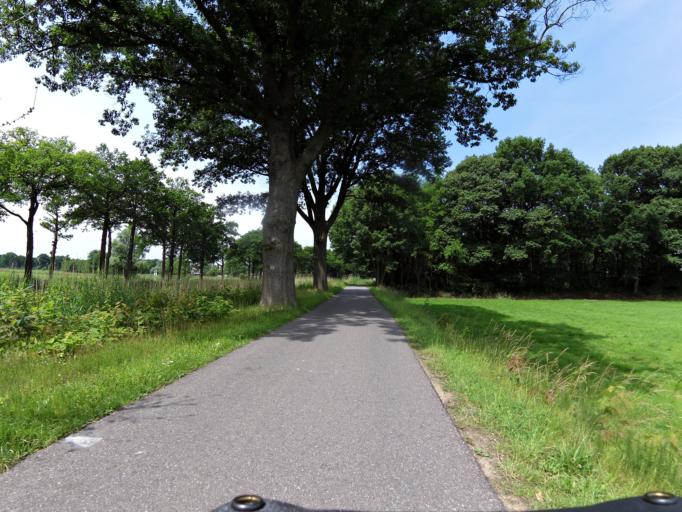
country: NL
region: Gelderland
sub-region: Gemeente Brummen
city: Eerbeek
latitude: 52.1260
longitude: 6.0487
